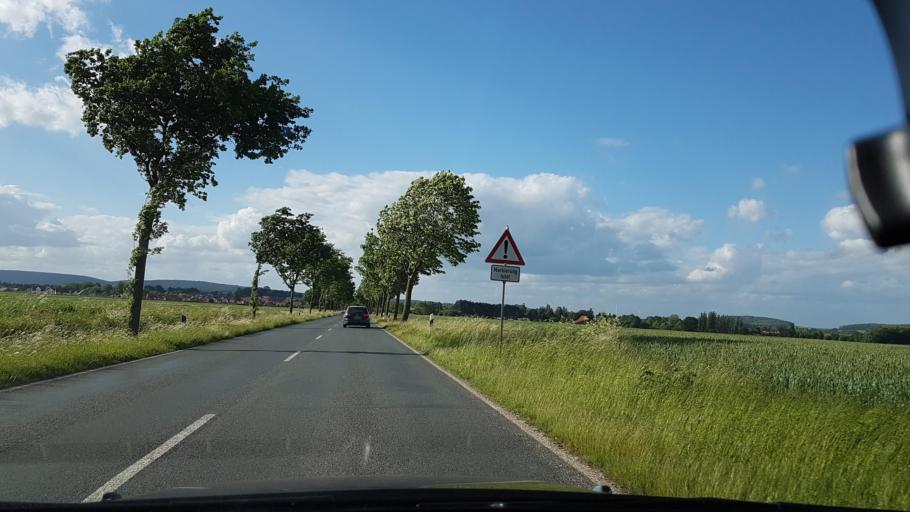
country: DE
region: Lower Saxony
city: Elze
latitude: 52.1592
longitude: 9.6616
